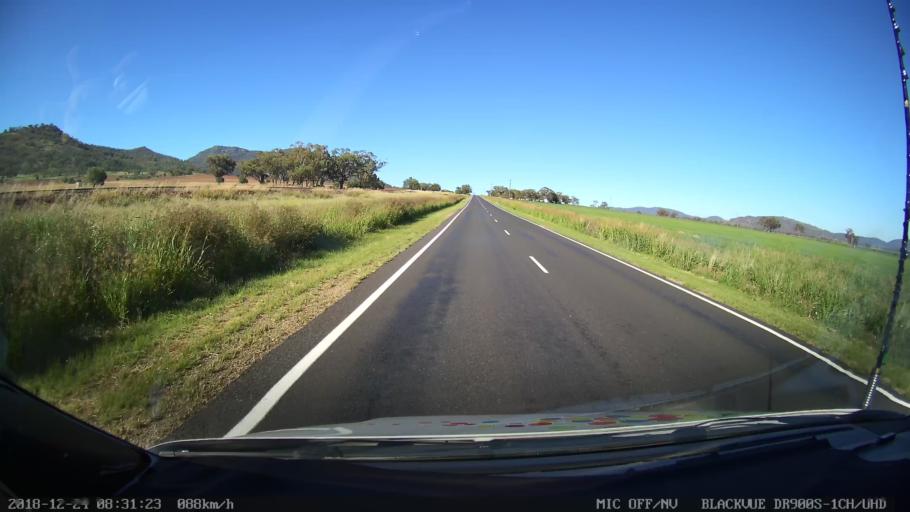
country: AU
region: New South Wales
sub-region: Tamworth Municipality
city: Phillip
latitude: -31.2732
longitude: 150.7122
